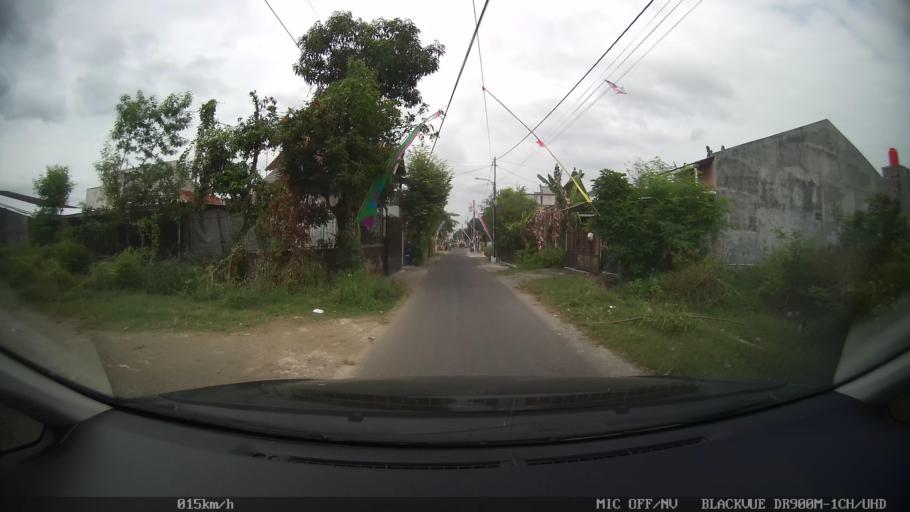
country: ID
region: Daerah Istimewa Yogyakarta
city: Depok
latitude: -7.8135
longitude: 110.4192
